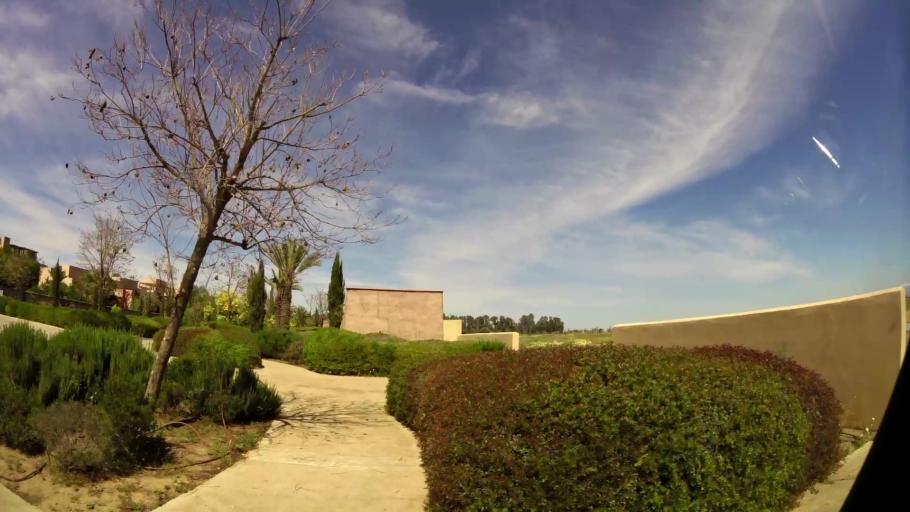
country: MA
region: Marrakech-Tensift-Al Haouz
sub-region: Marrakech
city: Marrakesh
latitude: 31.5997
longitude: -7.9488
